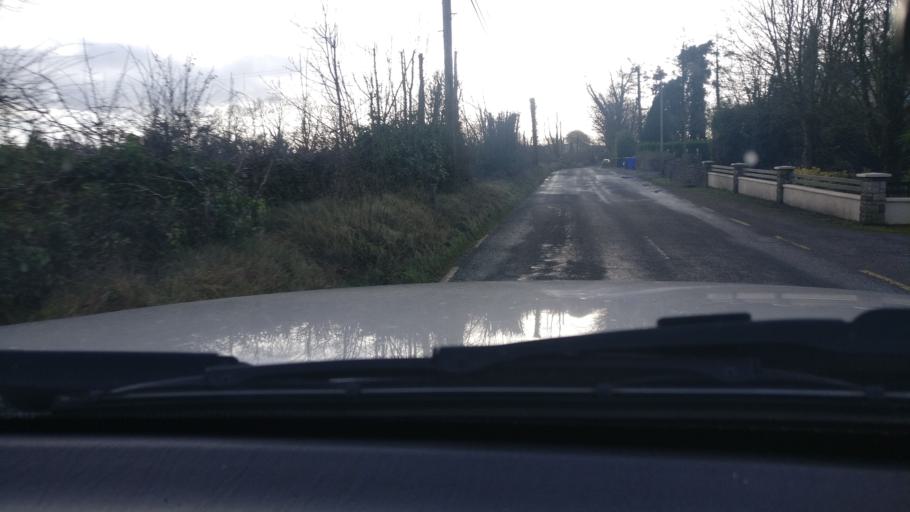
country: IE
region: Connaught
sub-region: County Galway
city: Ballinasloe
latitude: 53.2438
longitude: -8.2675
